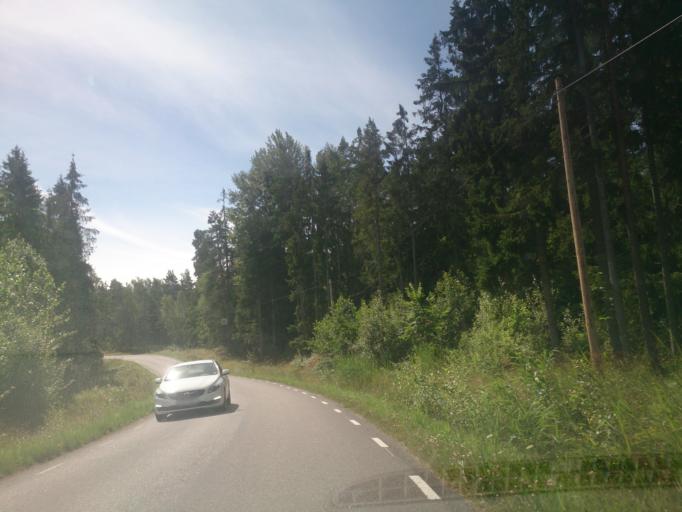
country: SE
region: OEstergoetland
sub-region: Valdemarsviks Kommun
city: Valdemarsvik
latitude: 58.3261
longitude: 16.6417
